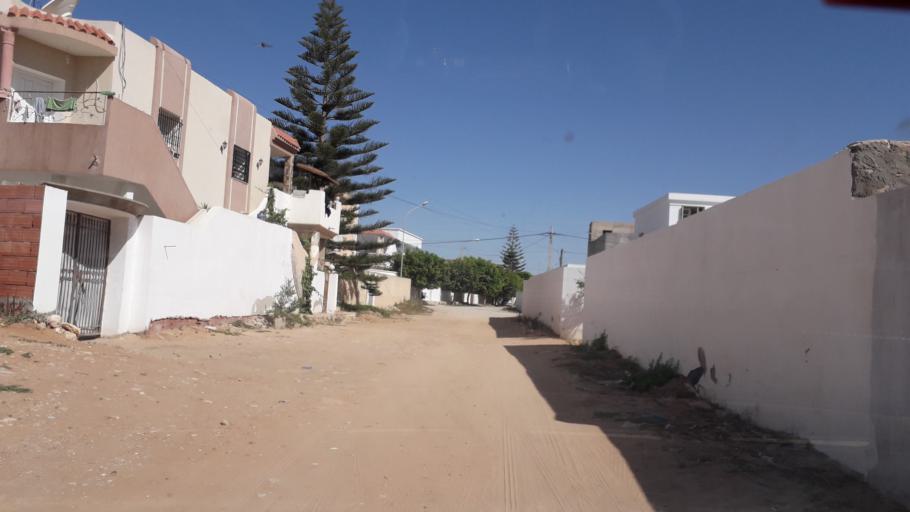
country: TN
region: Safaqis
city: Al Qarmadah
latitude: 34.8085
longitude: 10.7648
